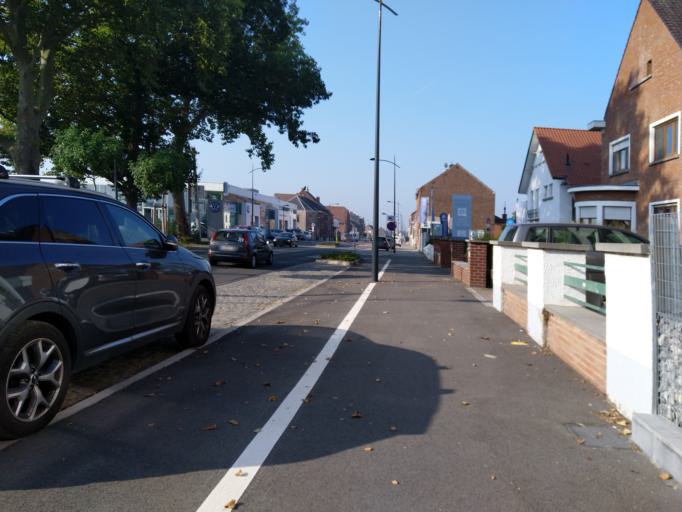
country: BE
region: Wallonia
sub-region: Province du Hainaut
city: Soignies
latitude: 50.5842
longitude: 4.0821
